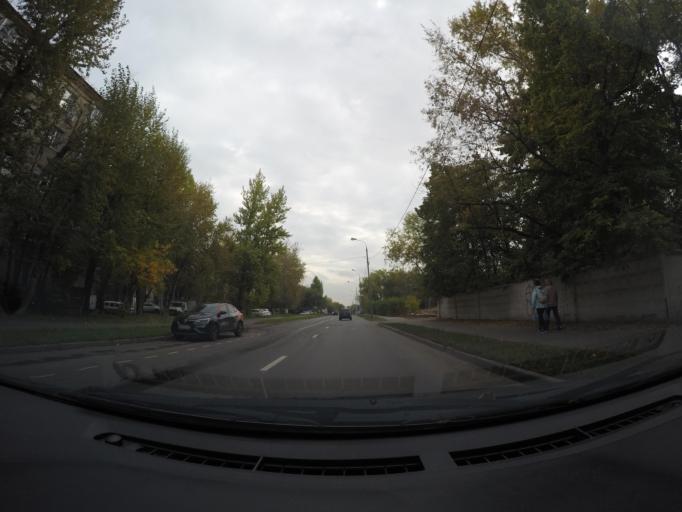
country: RU
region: Moscow
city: Lefortovo
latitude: 55.7609
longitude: 37.7311
